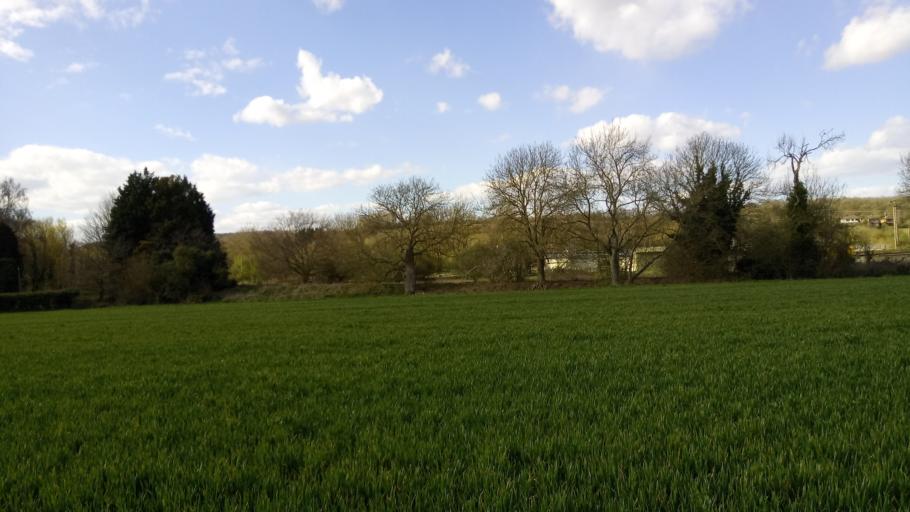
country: GB
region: England
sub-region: Kent
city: Chartham
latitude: 51.2546
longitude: 1.0244
